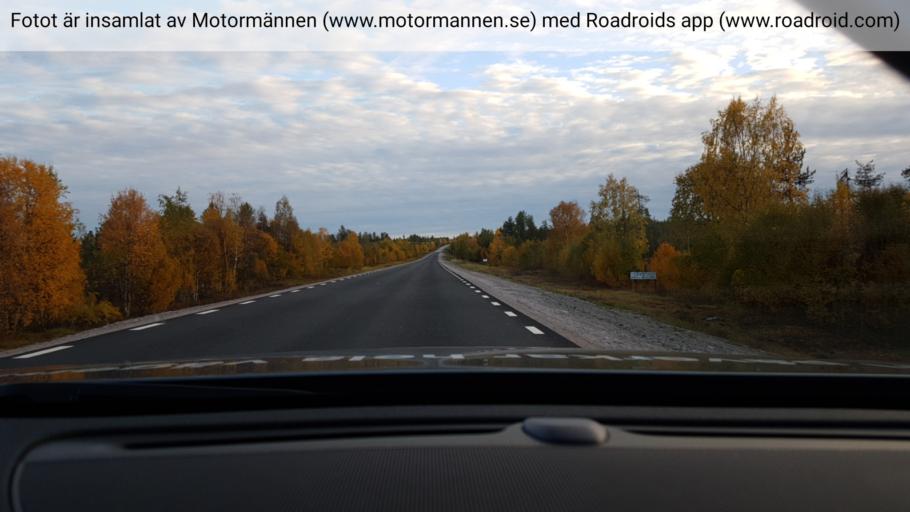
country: SE
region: Norrbotten
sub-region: Jokkmokks Kommun
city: Jokkmokk
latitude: 66.4499
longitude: 19.6921
